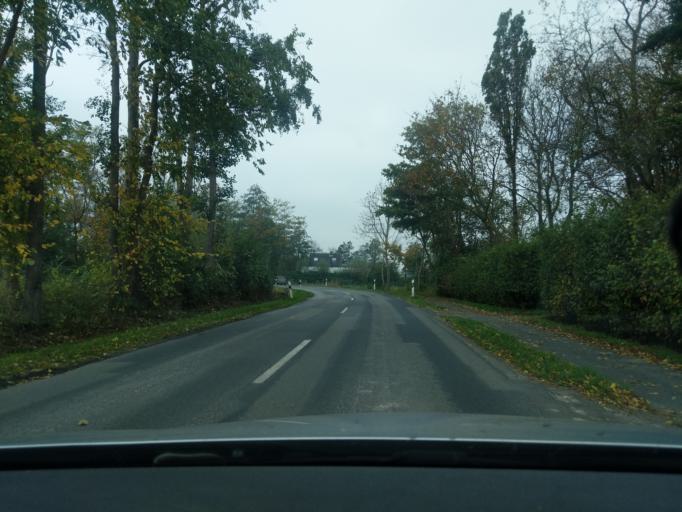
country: DE
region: Lower Saxony
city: Otterndorf
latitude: 53.8145
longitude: 8.8784
